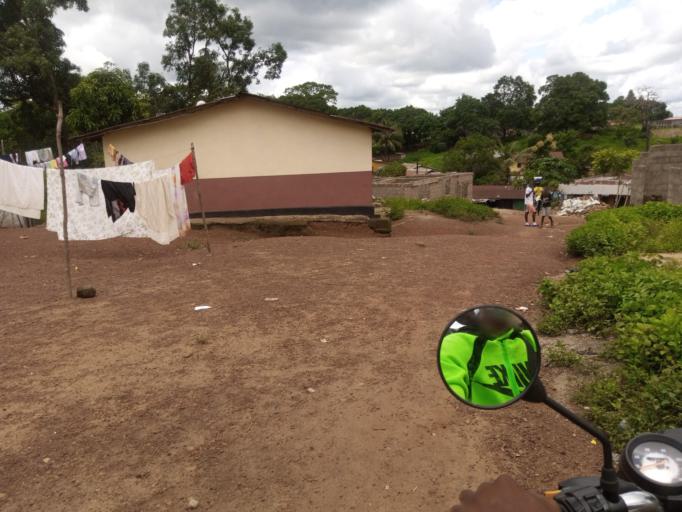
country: SL
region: Northern Province
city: Port Loko
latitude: 8.7646
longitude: -12.7836
